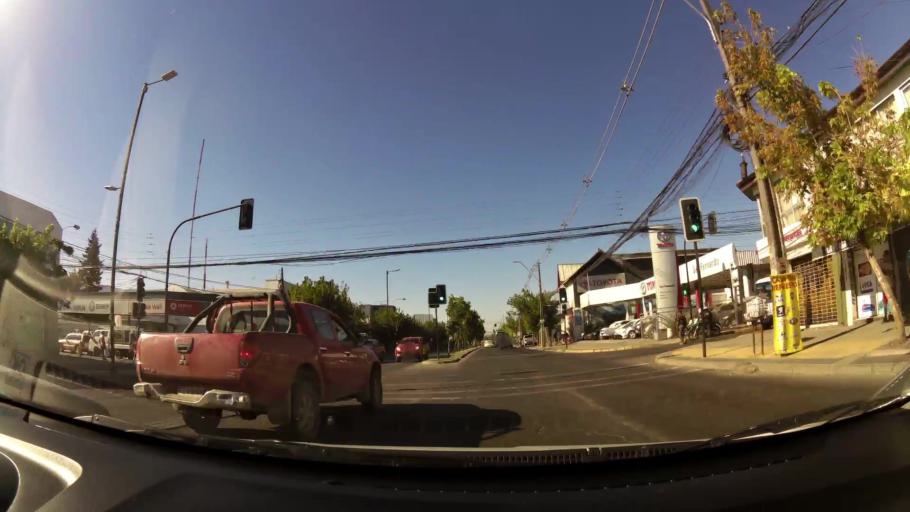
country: CL
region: O'Higgins
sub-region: Provincia de Colchagua
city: Chimbarongo
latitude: -34.5905
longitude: -70.9862
